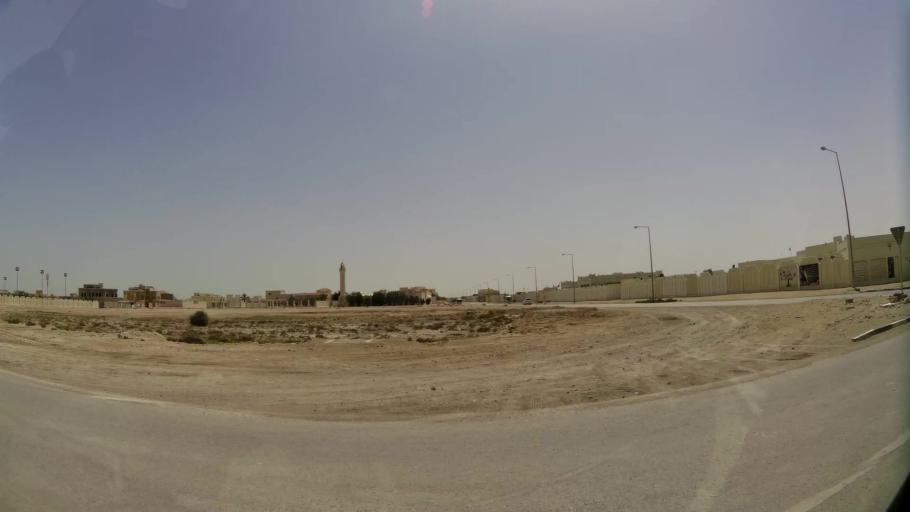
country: QA
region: Baladiyat Umm Salal
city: Umm Salal Muhammad
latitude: 25.3981
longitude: 51.4471
